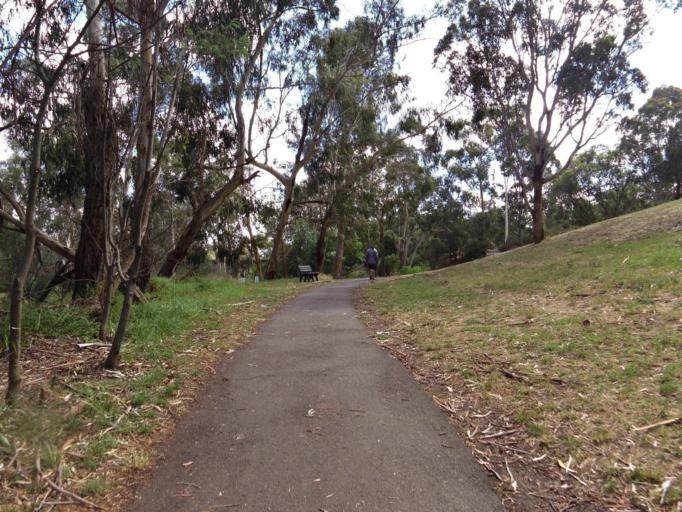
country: AU
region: Victoria
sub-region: Nillumbik
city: Eltham
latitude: -37.7174
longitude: 145.1442
